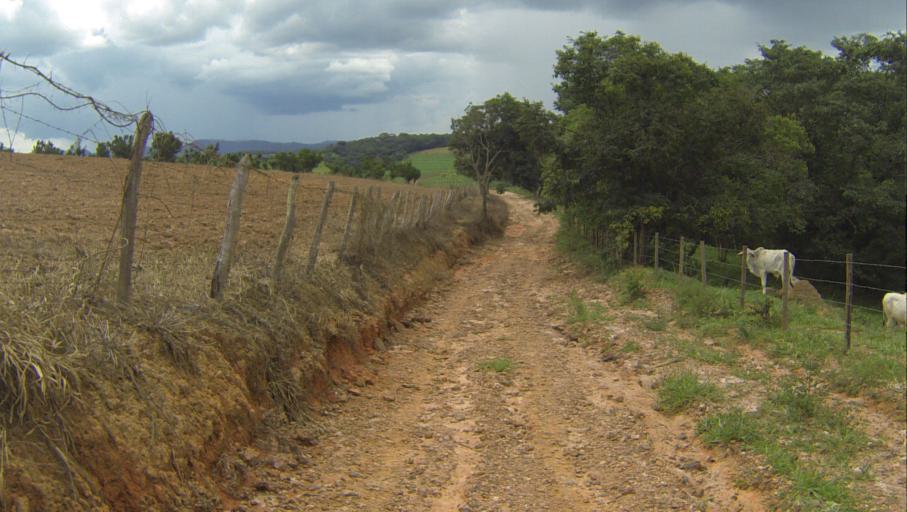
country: BR
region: Minas Gerais
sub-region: Brumadinho
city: Brumadinho
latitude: -20.1505
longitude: -44.1199
